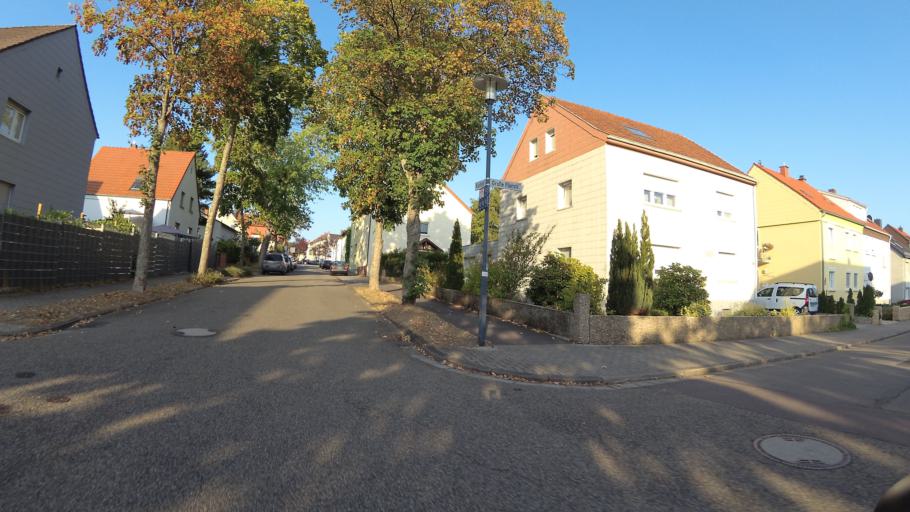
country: DE
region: Saarland
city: Sankt Ingbert
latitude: 49.2832
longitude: 7.1070
